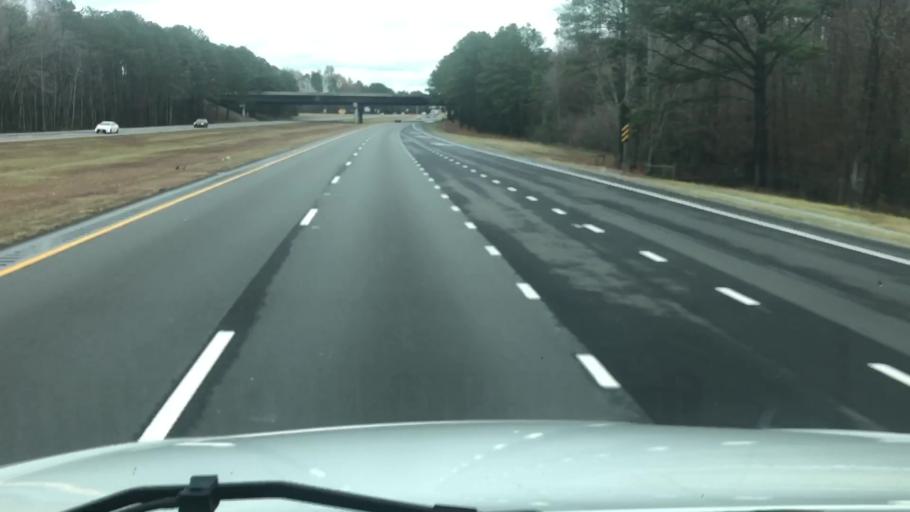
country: US
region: North Carolina
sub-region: Cumberland County
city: Eastover
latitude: 35.0863
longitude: -78.7845
